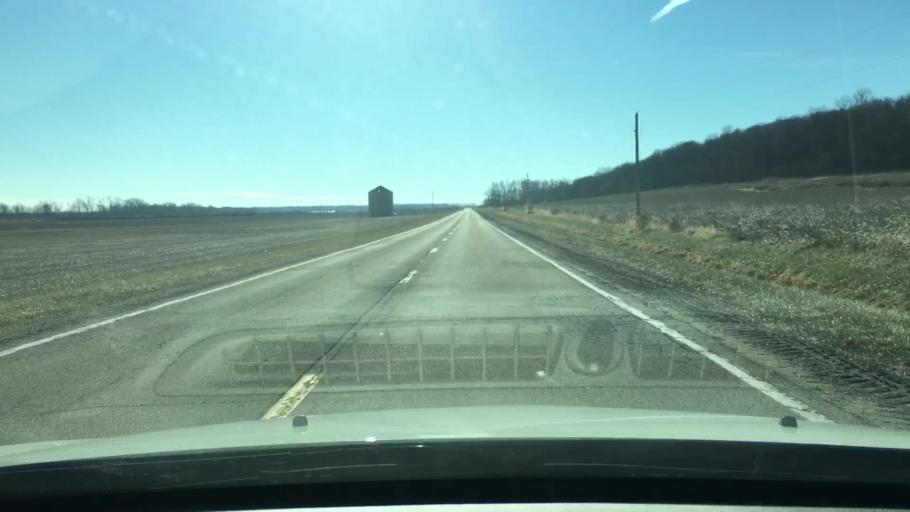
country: US
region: Illinois
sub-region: Mason County
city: Havana
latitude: 40.2713
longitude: -90.1756
